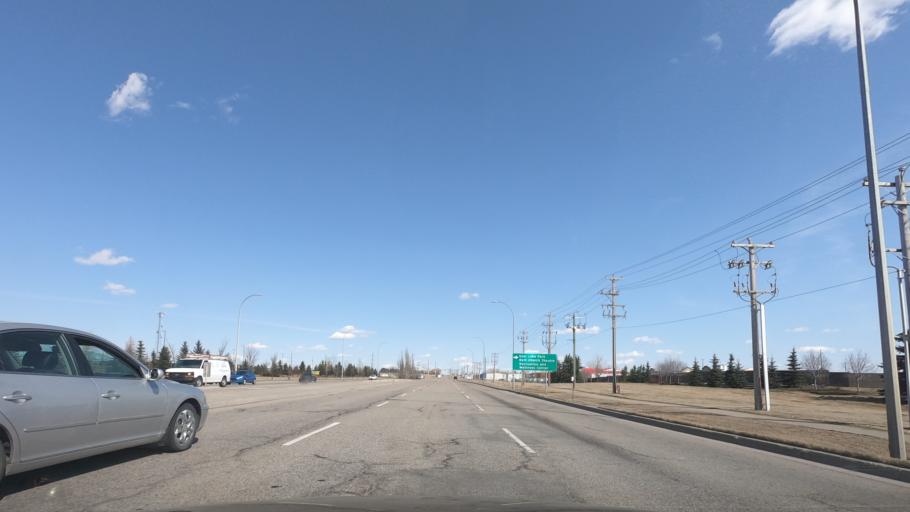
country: CA
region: Alberta
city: Airdrie
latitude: 51.2999
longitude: -113.9945
